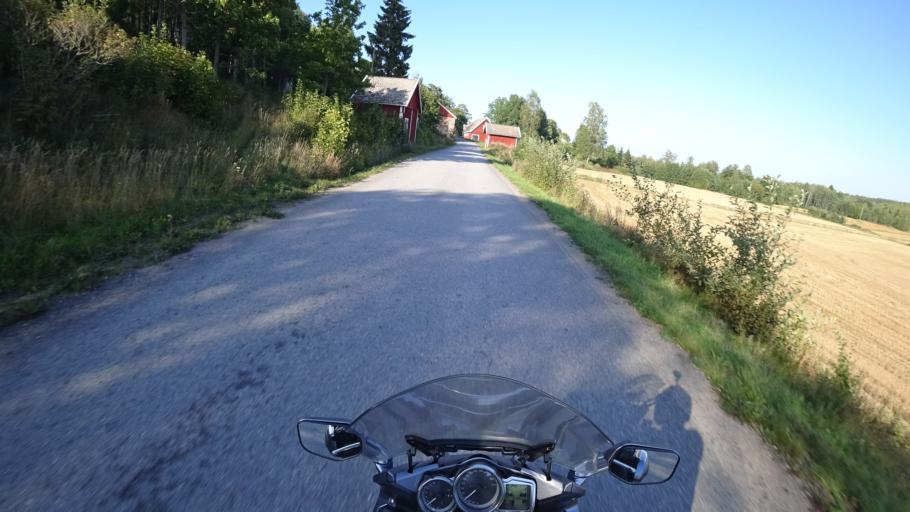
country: FI
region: Uusimaa
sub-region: Helsinki
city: Sammatti
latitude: 60.2986
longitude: 23.7561
